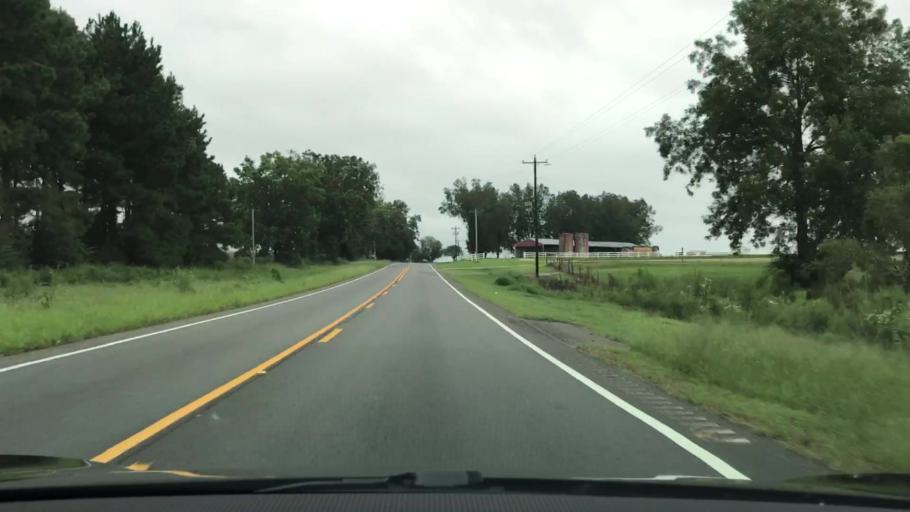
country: US
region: Alabama
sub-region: Covington County
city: Opp
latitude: 31.2333
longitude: -86.1619
